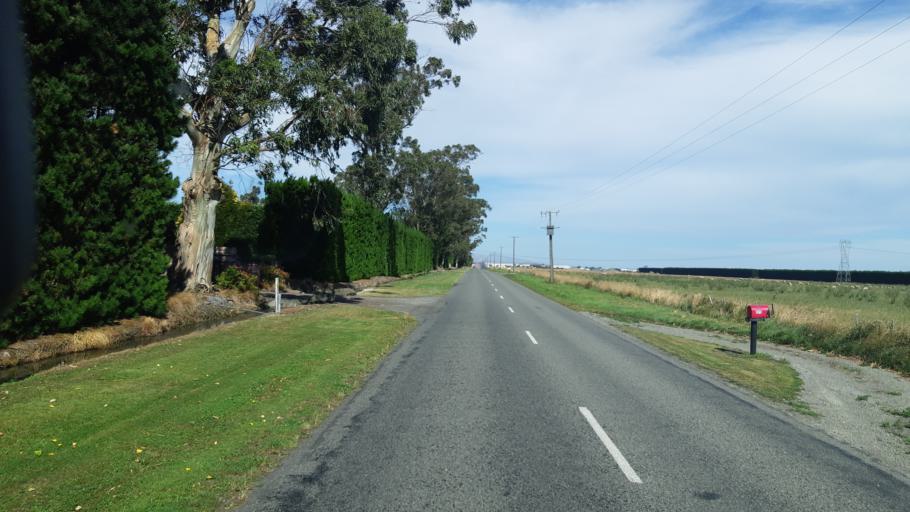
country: NZ
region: Canterbury
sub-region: Selwyn District
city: Rolleston
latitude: -43.5669
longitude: 172.3653
